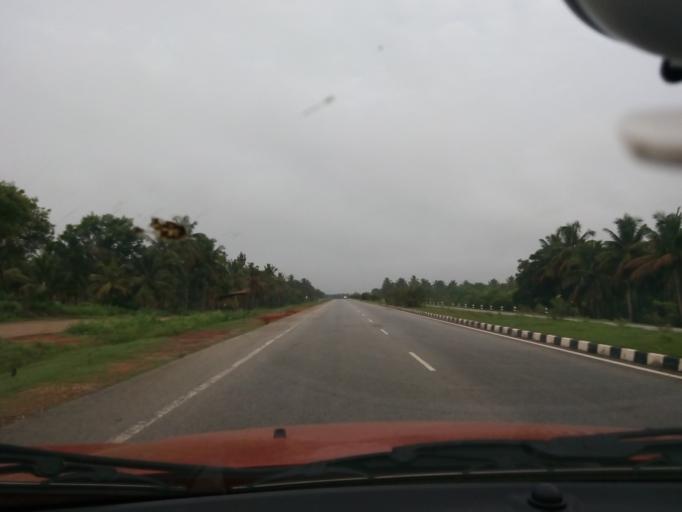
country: IN
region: Karnataka
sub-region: Tumkur
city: Kunigal
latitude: 13.0052
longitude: 76.9875
